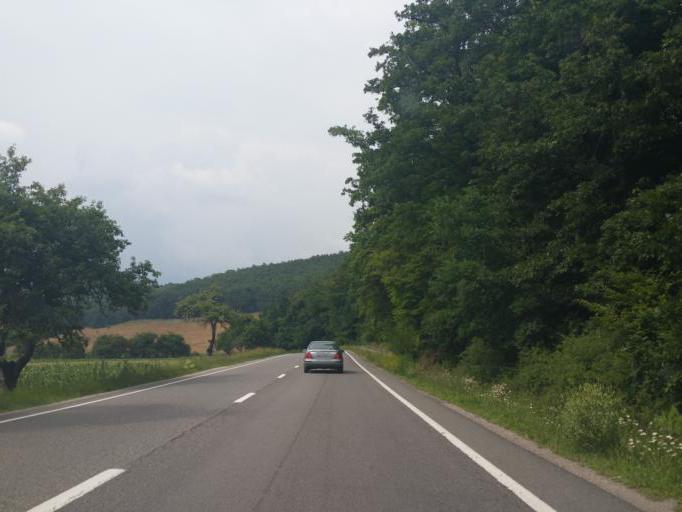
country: RO
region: Salaj
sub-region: Comuna Romanasi
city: Romanasi
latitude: 47.1157
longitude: 23.1653
